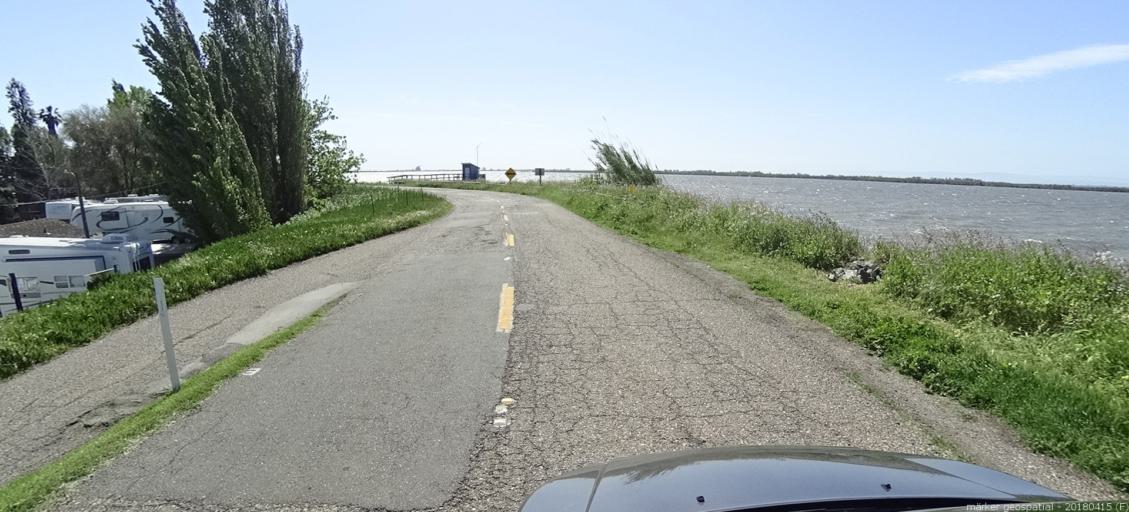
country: US
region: California
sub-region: Contra Costa County
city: Bethel Island
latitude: 38.1038
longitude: -121.5921
